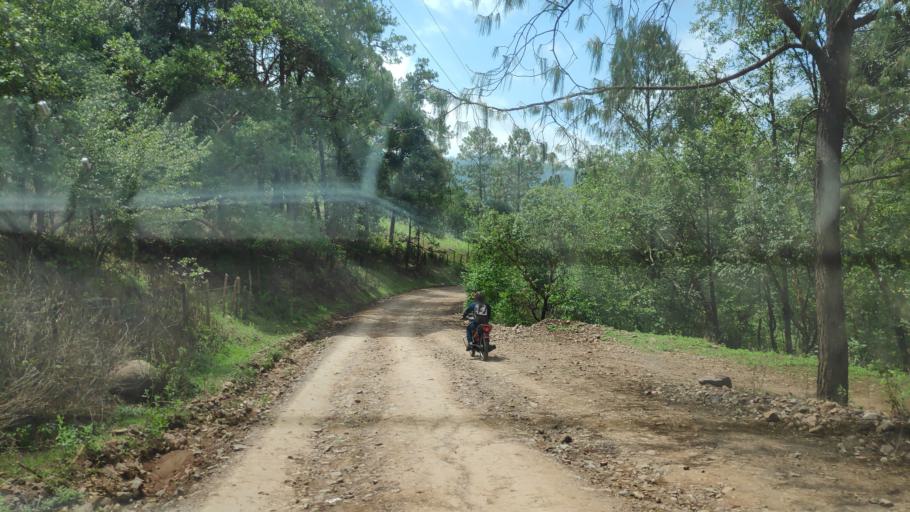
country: MX
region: Sinaloa
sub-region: Sinaloa
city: Bacubirito
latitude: 25.8571
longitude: -107.5877
